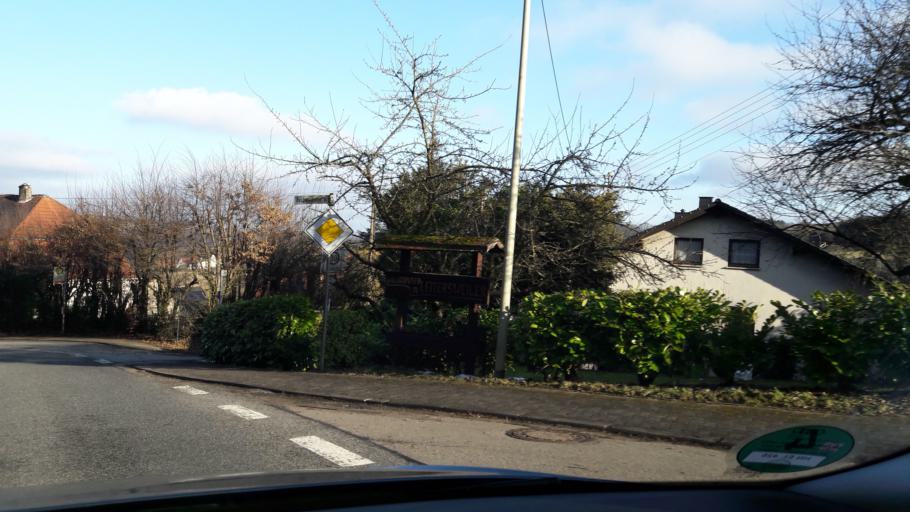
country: DE
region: Saarland
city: Sankt Wendel
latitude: 49.4904
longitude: 7.2047
